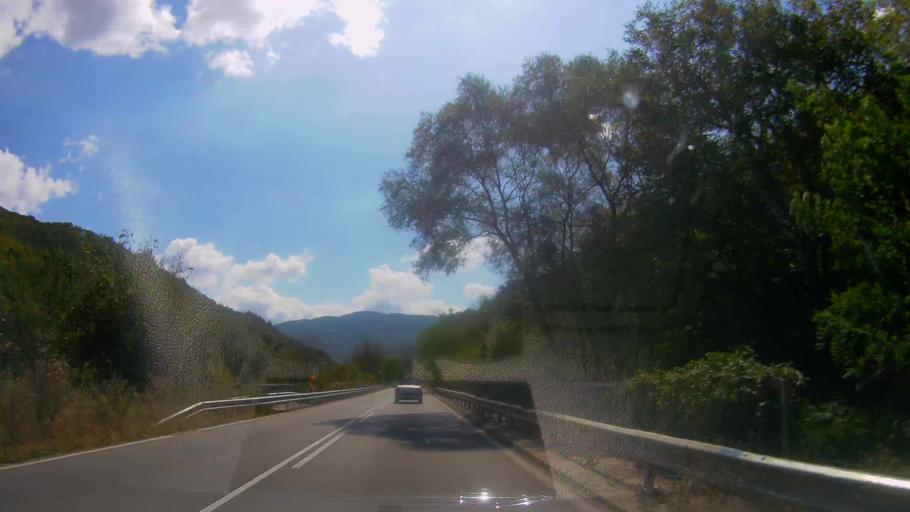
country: BG
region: Stara Zagora
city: Gurkovo
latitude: 42.7320
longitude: 25.7119
